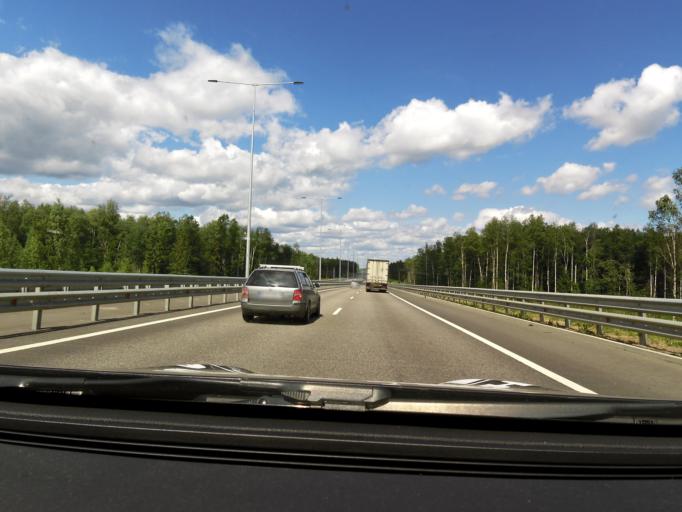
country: RU
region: Tverskaya
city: Vyshniy Volochek
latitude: 57.3898
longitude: 34.5514
